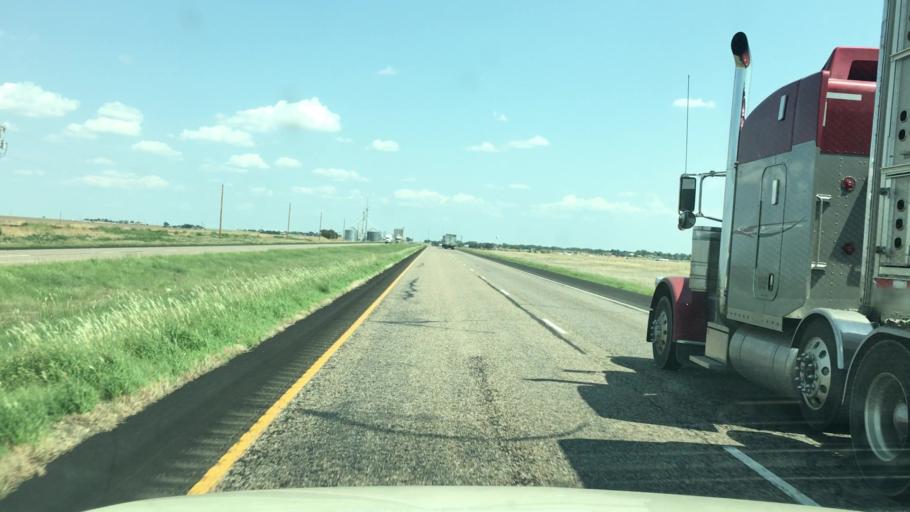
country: US
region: Texas
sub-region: Armstrong County
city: Claude
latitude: 35.1227
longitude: -101.3900
